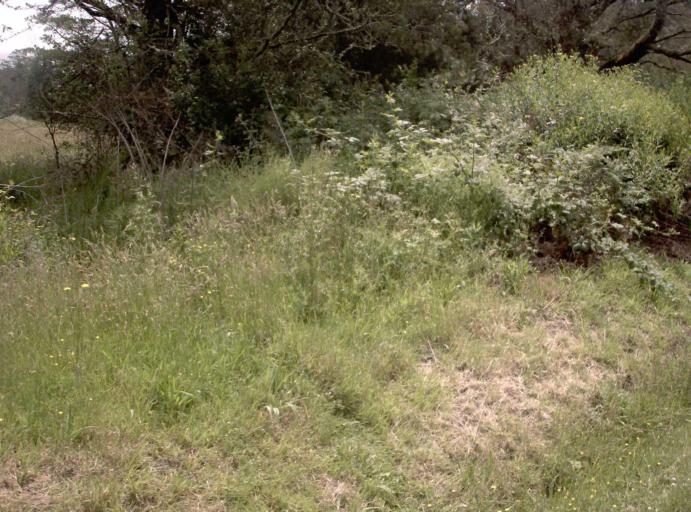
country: AU
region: Victoria
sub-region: Latrobe
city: Traralgon
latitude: -38.4272
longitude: 146.5658
